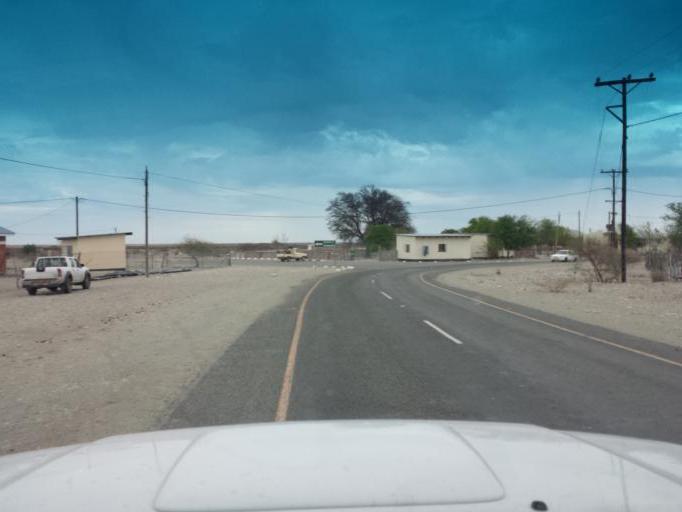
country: BW
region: Central
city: Mopipi
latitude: -21.2027
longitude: 24.8563
